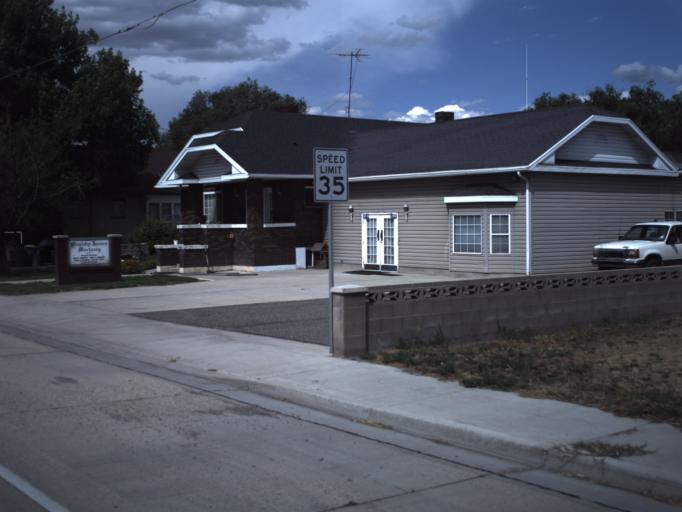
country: US
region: Utah
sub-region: Sevier County
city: Salina
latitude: 38.9593
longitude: -111.8600
